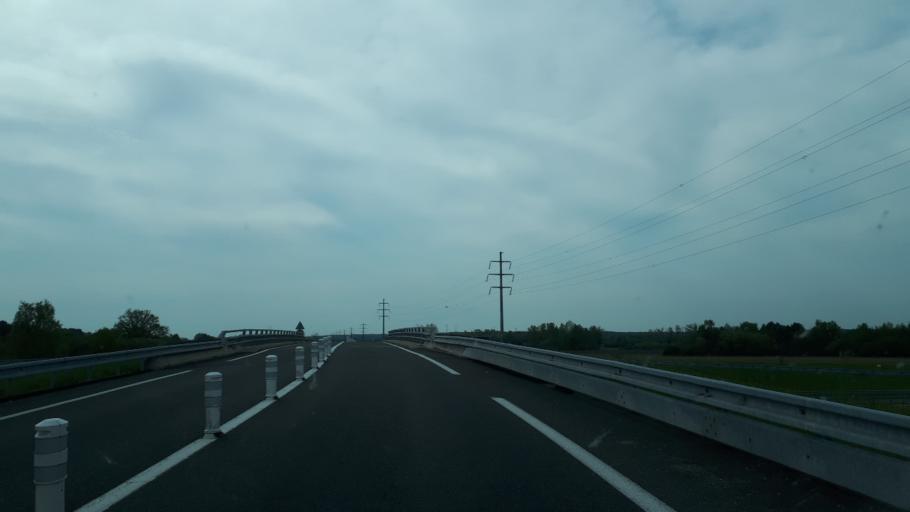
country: FR
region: Centre
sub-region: Departement du Loir-et-Cher
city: Chatillon-sur-Cher
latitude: 47.3288
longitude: 1.4993
